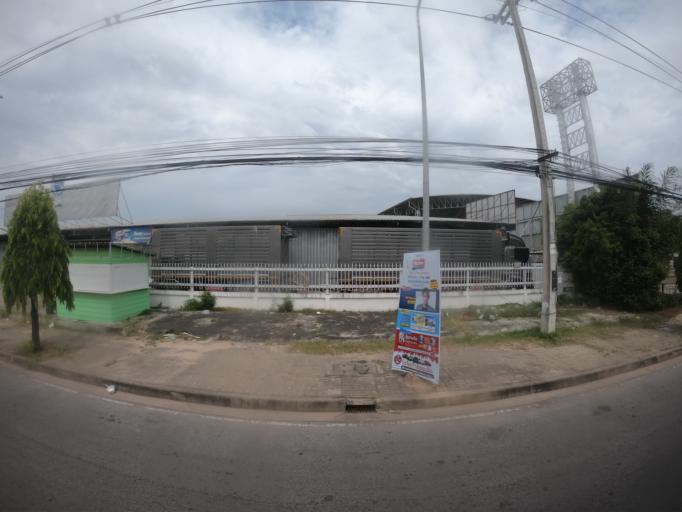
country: TH
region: Roi Et
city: Roi Et
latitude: 16.0578
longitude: 103.6338
